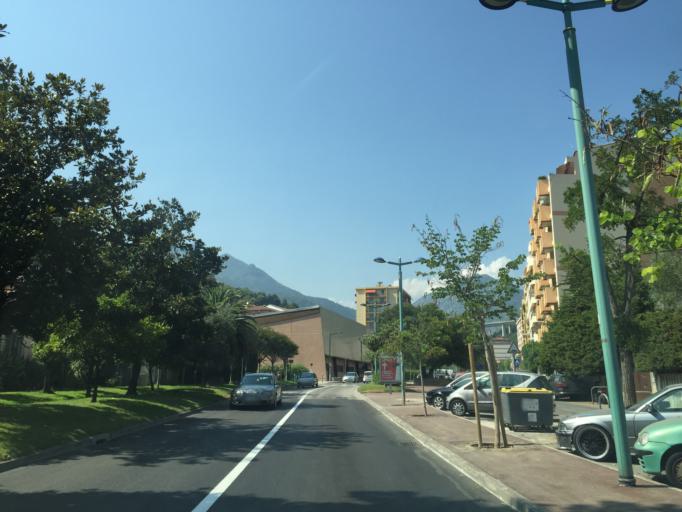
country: FR
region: Provence-Alpes-Cote d'Azur
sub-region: Departement des Alpes-Maritimes
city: Menton
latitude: 43.7879
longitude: 7.4933
